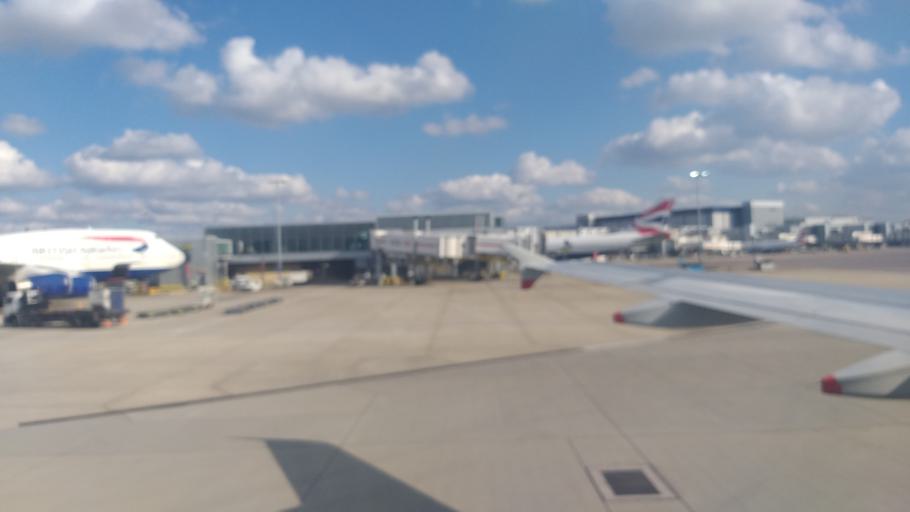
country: GB
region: England
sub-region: Greater London
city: West Drayton
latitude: 51.4733
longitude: -0.4672
